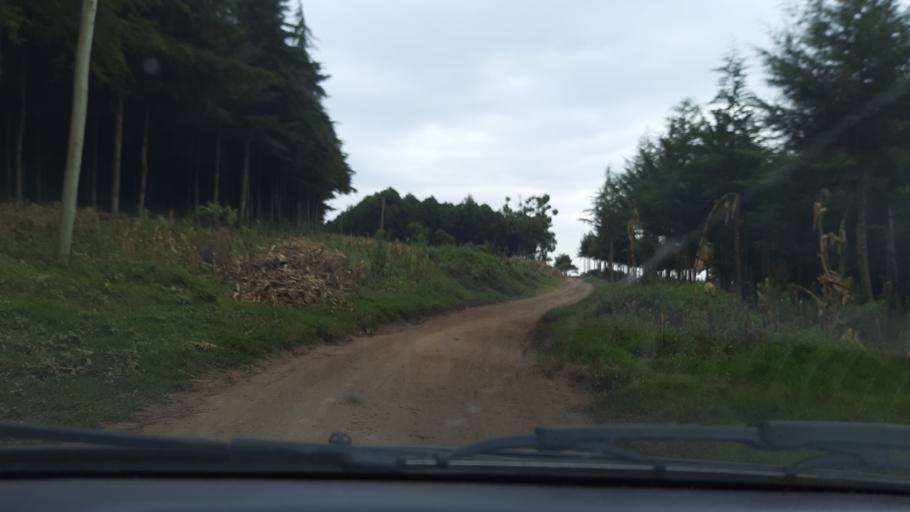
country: TZ
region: Kilimanjaro
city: Moshi
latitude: -2.9326
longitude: 37.4667
